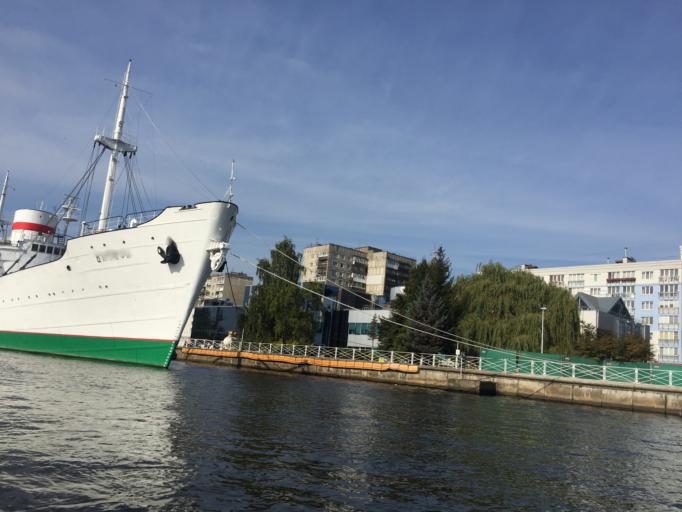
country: RU
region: Kaliningrad
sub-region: Gorod Kaliningrad
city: Kaliningrad
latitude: 54.7059
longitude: 20.5011
